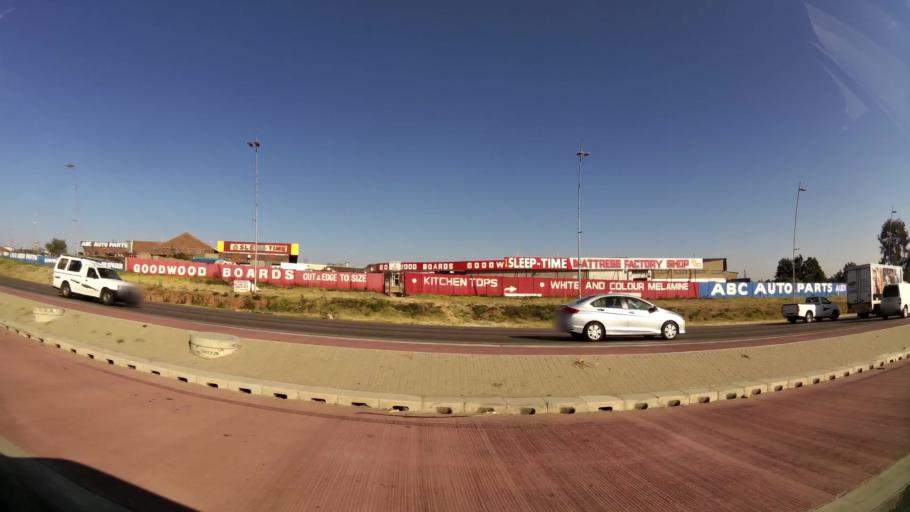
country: ZA
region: Gauteng
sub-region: City of Johannesburg Metropolitan Municipality
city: Modderfontein
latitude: -26.0654
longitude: 28.1857
